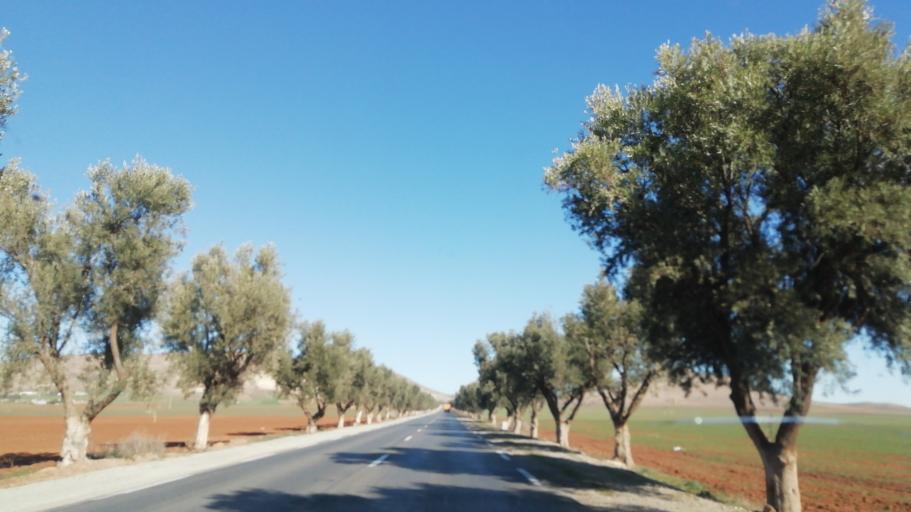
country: DZ
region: Mascara
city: Mascara
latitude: 35.2262
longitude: 0.1144
